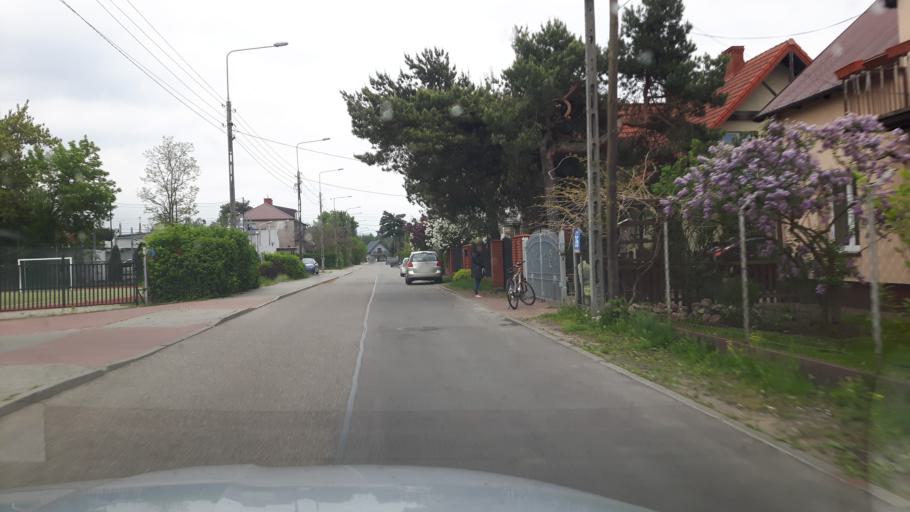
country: PL
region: Masovian Voivodeship
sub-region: Warszawa
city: Rembertow
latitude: 52.2506
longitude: 21.1672
